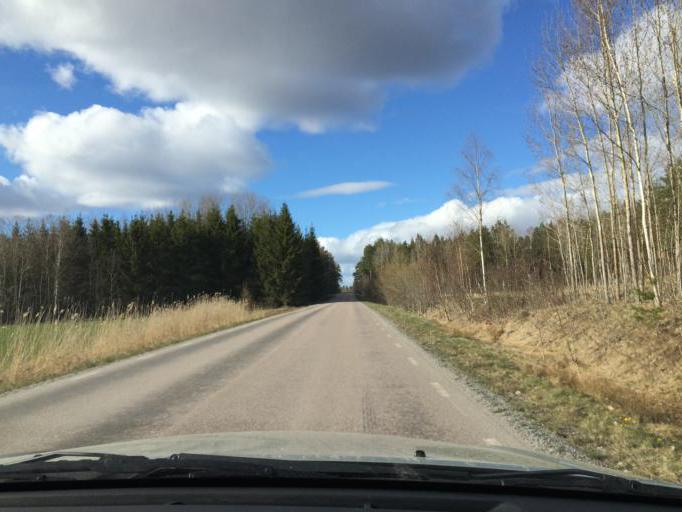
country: SE
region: Soedermanland
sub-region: Eskilstuna Kommun
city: Hallbybrunn
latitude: 59.4189
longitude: 16.4359
